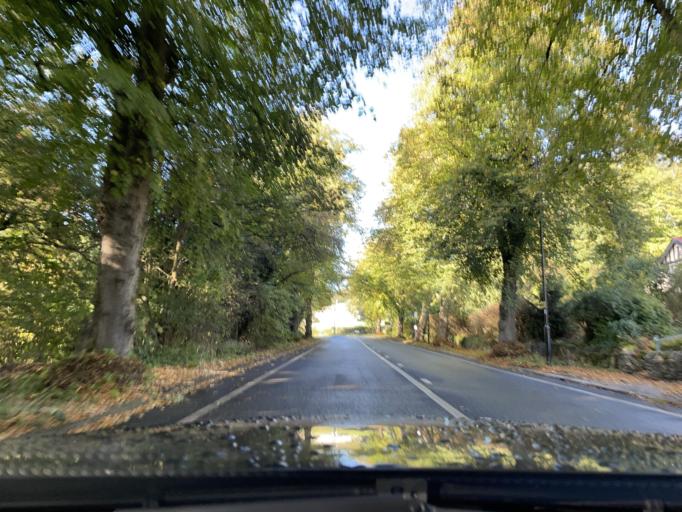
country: GB
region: England
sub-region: Sheffield
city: Oughtibridge
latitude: 53.3841
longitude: -1.5478
